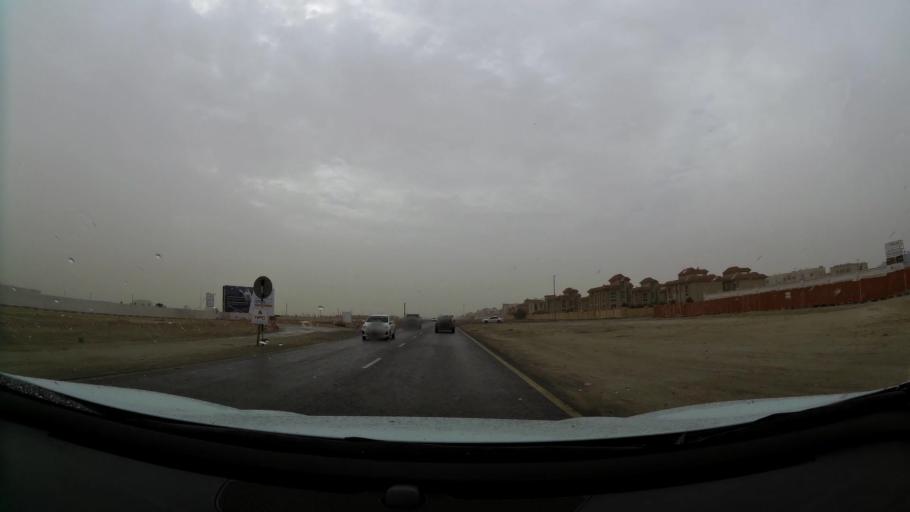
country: AE
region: Abu Dhabi
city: Abu Dhabi
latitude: 24.4364
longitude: 54.6029
